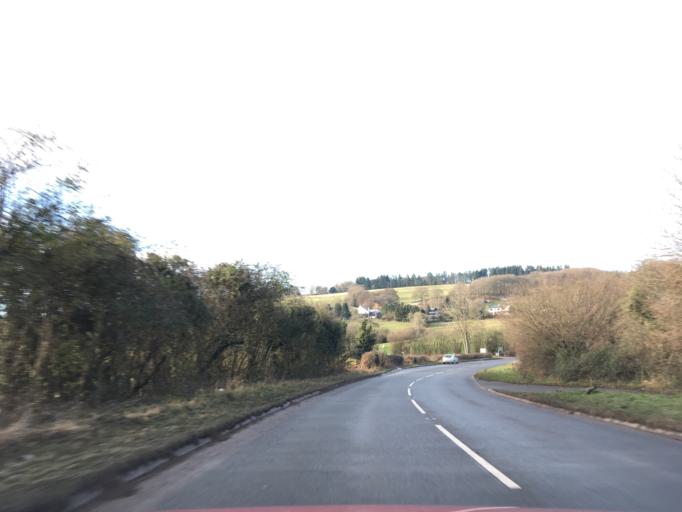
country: GB
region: Wales
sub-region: Monmouthshire
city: Monmouth
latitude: 51.8082
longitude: -2.6707
